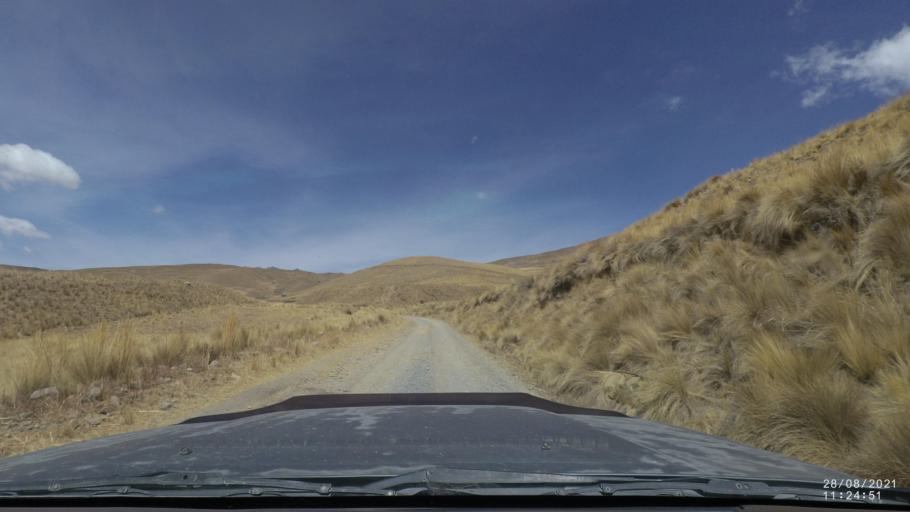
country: BO
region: Cochabamba
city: Sipe Sipe
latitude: -17.1692
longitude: -66.3520
